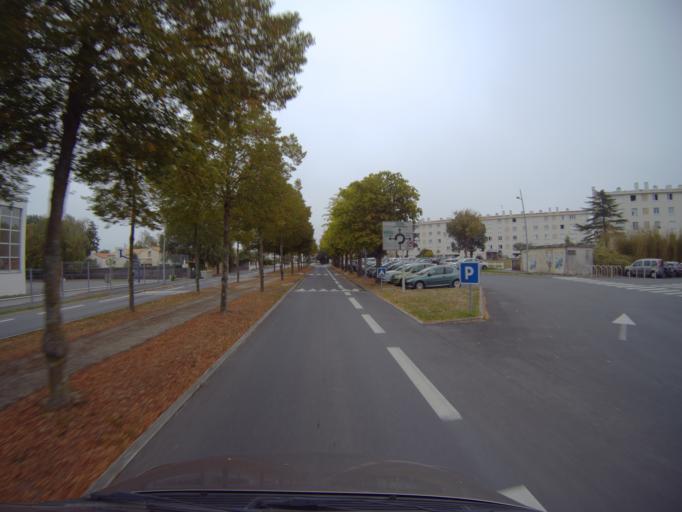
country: FR
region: Pays de la Loire
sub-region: Departement de la Vendee
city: Montaigu
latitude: 46.9817
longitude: -1.3077
